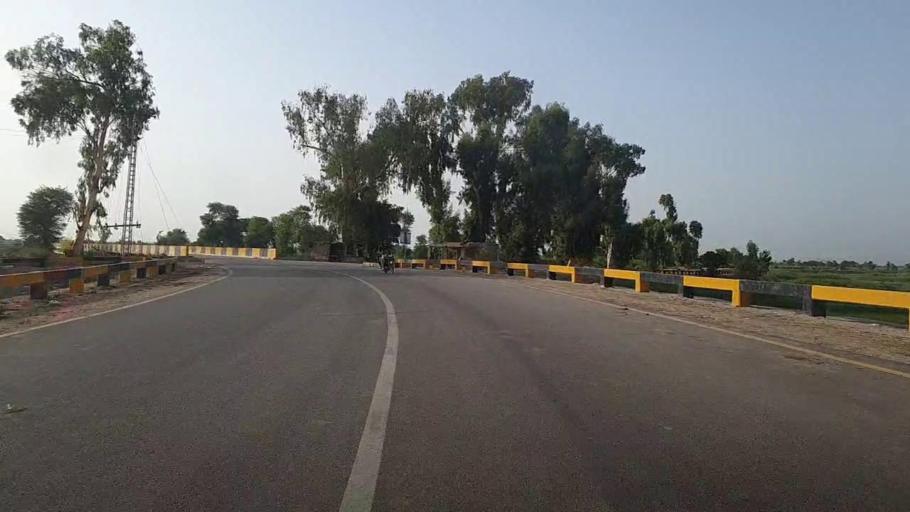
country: PK
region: Sindh
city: Naushahro Firoz
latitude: 26.7930
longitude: 68.1448
